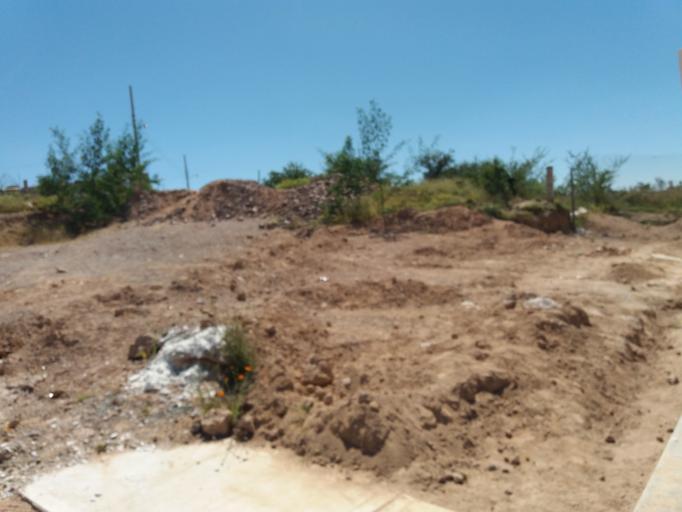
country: MX
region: Aguascalientes
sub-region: Aguascalientes
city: Aguascalientes
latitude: 21.8675
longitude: -102.2294
